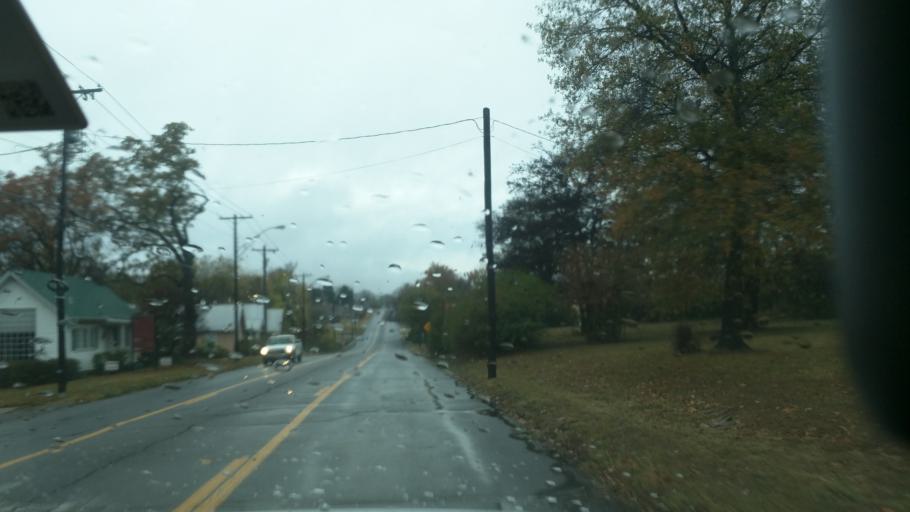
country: US
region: Arkansas
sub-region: Franklin County
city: Ozark
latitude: 35.4878
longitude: -93.8342
